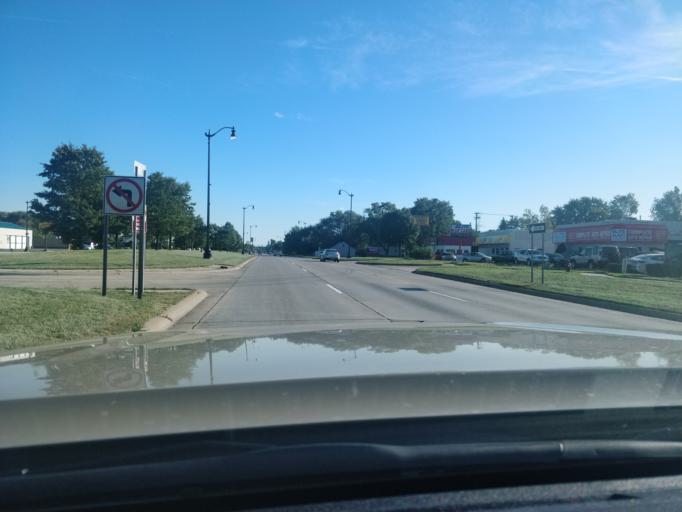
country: US
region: Michigan
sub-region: Wayne County
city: Taylor
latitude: 42.2035
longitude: -83.2686
